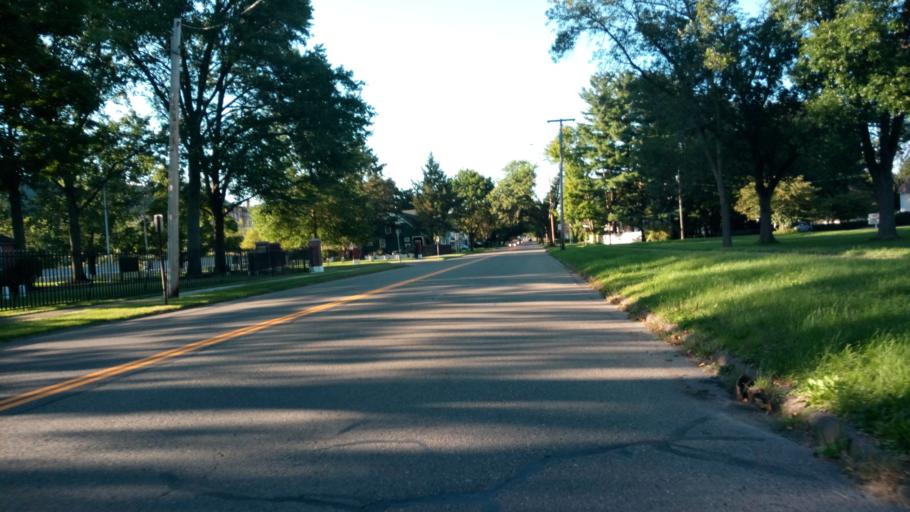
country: US
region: New York
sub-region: Chemung County
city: Elmira Heights
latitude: 42.1105
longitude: -76.8263
